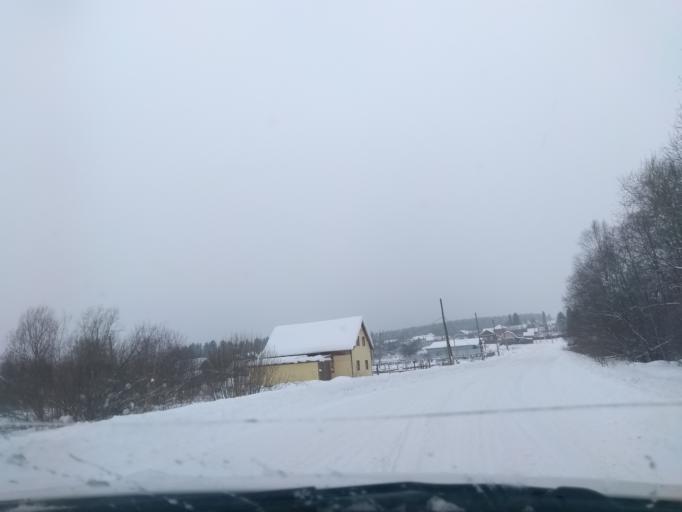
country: RU
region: Perm
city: Sylva
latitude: 57.8350
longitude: 56.6799
